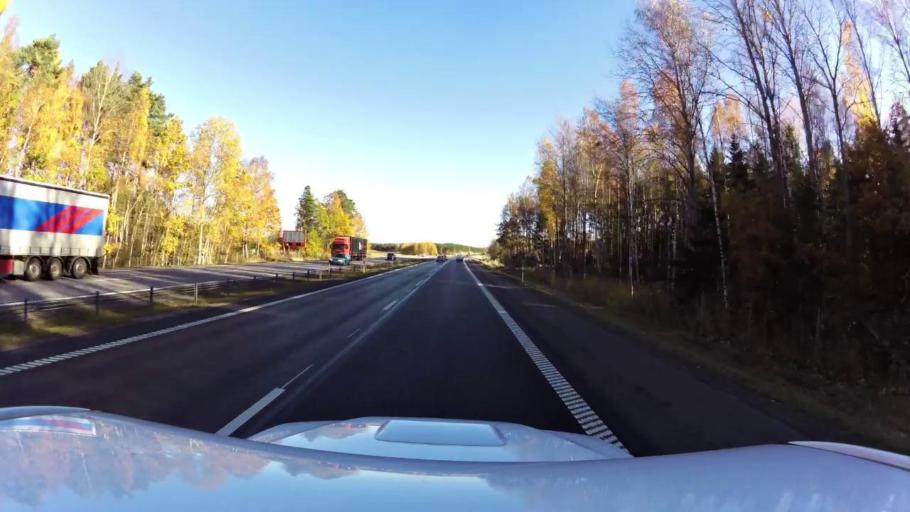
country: SE
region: OEstergoetland
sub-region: Linkopings Kommun
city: Vikingstad
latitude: 58.3823
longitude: 15.3584
